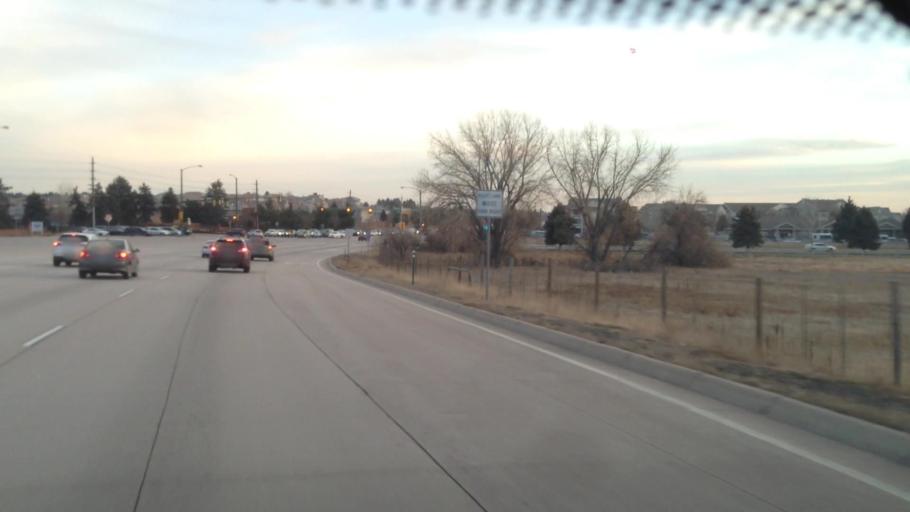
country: US
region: Colorado
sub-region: Arapahoe County
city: Dove Valley
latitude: 39.6116
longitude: -104.8120
